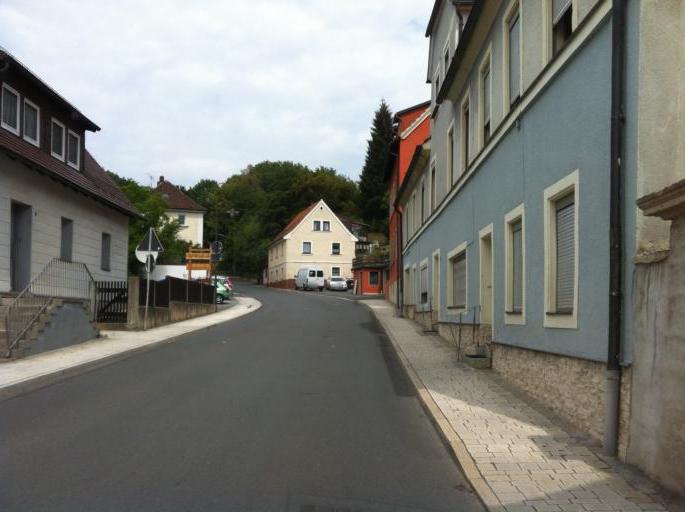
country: DE
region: Bavaria
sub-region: Upper Franconia
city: Goldkronach
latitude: 50.0083
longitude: 11.6853
